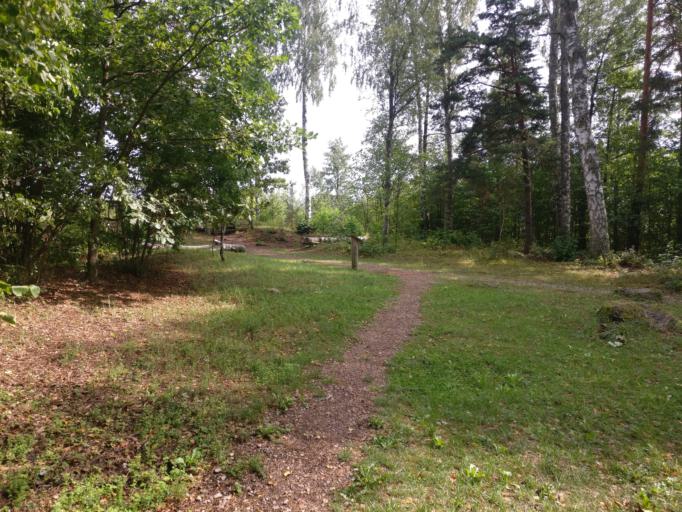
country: LV
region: Engure
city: Smarde
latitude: 56.9915
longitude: 23.4342
